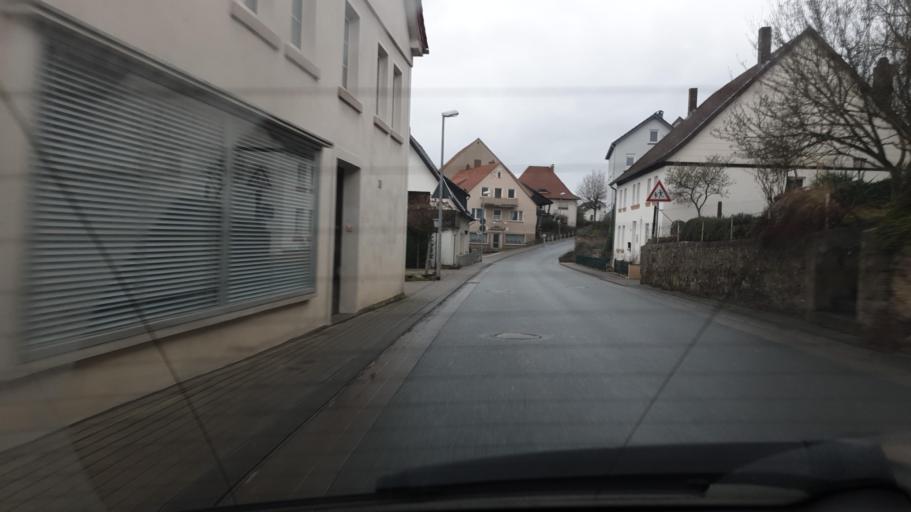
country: DE
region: North Rhine-Westphalia
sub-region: Regierungsbezirk Detmold
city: Detmold
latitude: 51.9792
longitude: 8.8457
